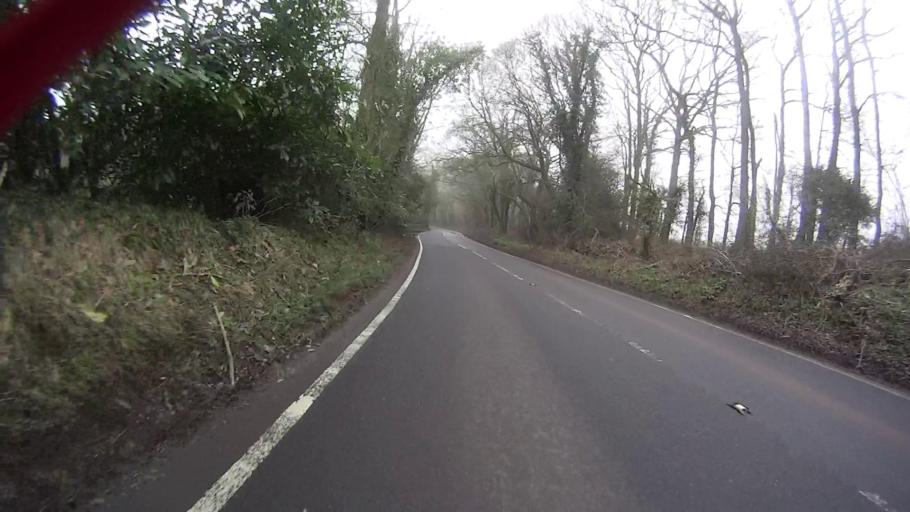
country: GB
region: England
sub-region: Surrey
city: Ockley
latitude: 51.1508
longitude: -0.3367
